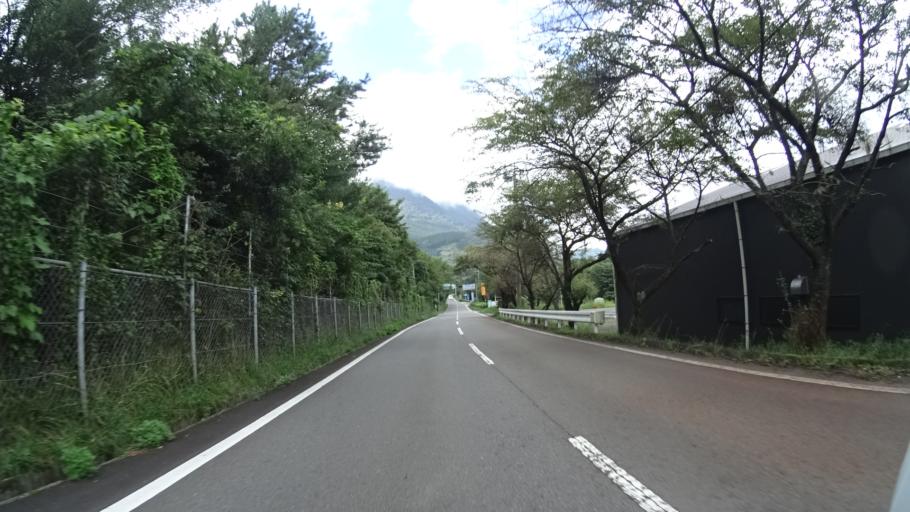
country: JP
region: Oita
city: Beppu
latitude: 33.3069
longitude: 131.4046
